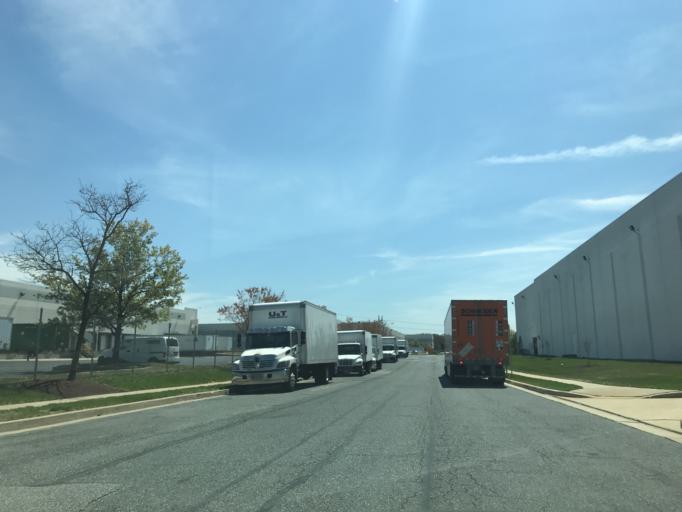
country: US
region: Maryland
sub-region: Baltimore County
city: Rossville
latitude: 39.3279
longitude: -76.4880
